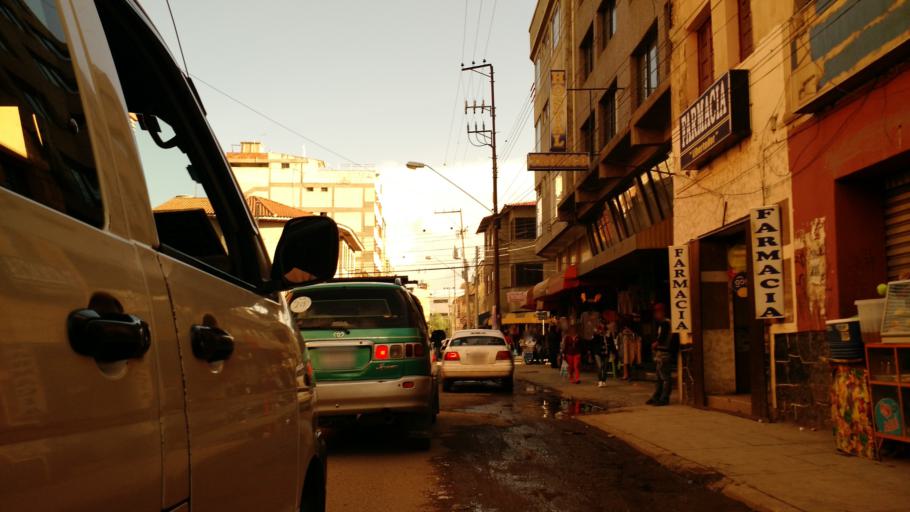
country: BO
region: Cochabamba
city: Cochabamba
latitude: -17.4003
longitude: -66.1563
